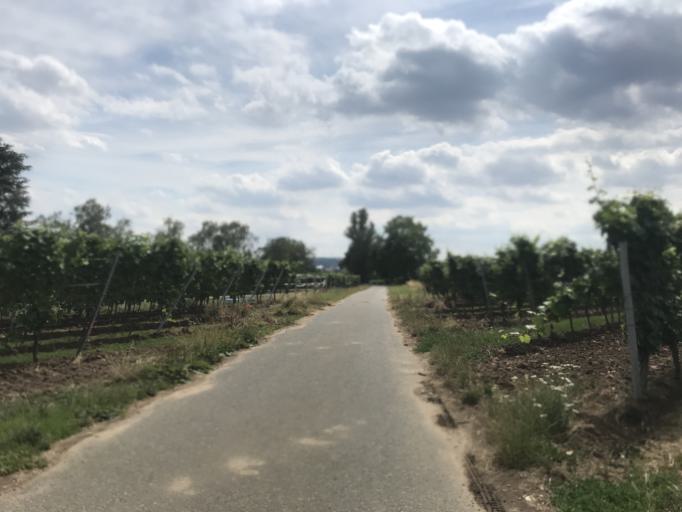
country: DE
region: Hesse
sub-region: Regierungsbezirk Darmstadt
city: Hochheim am Main
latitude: 50.0168
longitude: 8.3163
